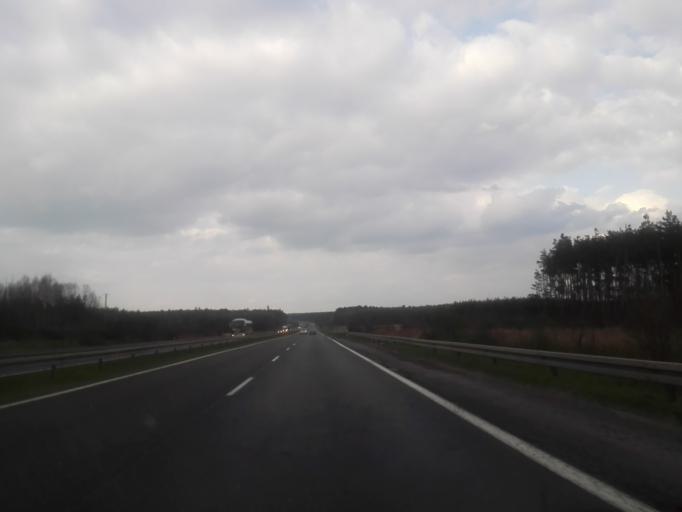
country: PL
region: Lodz Voivodeship
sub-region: Powiat radomszczanski
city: Gomunice
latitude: 51.1525
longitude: 19.4412
